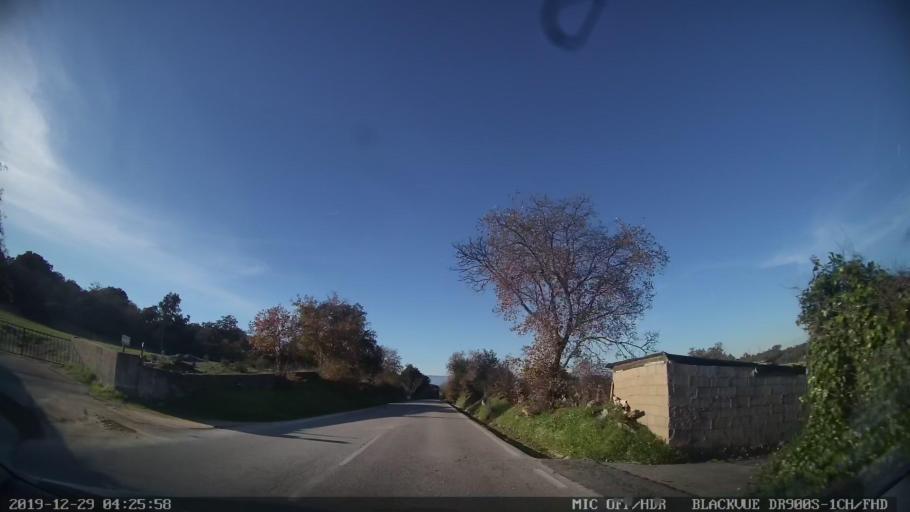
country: PT
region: Castelo Branco
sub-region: Idanha-A-Nova
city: Idanha-a-Nova
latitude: 39.9537
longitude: -7.2635
